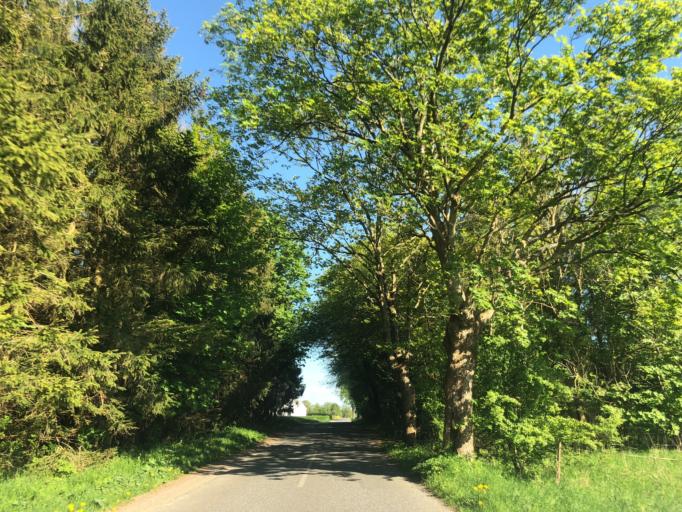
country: DK
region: Zealand
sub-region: Ringsted Kommune
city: Ringsted
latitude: 55.4590
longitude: 11.6903
